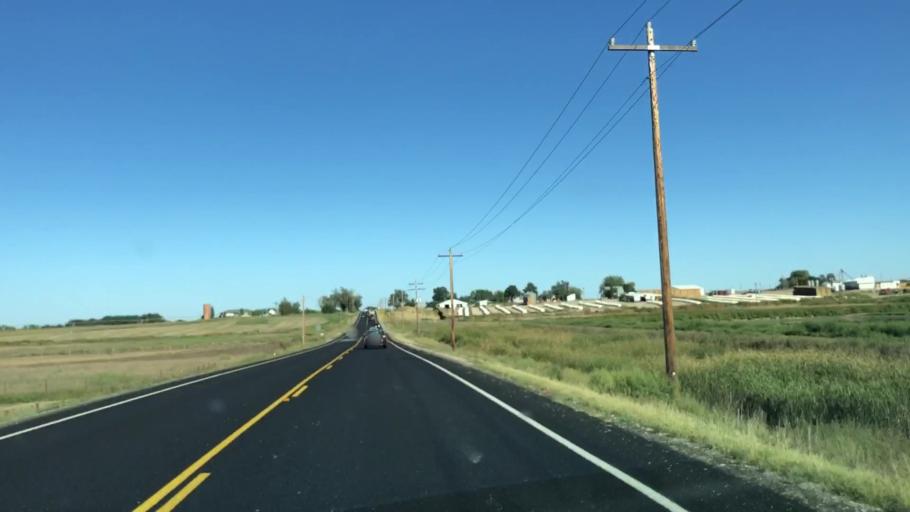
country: US
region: Colorado
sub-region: Larimer County
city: Loveland
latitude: 40.4656
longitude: -105.0321
